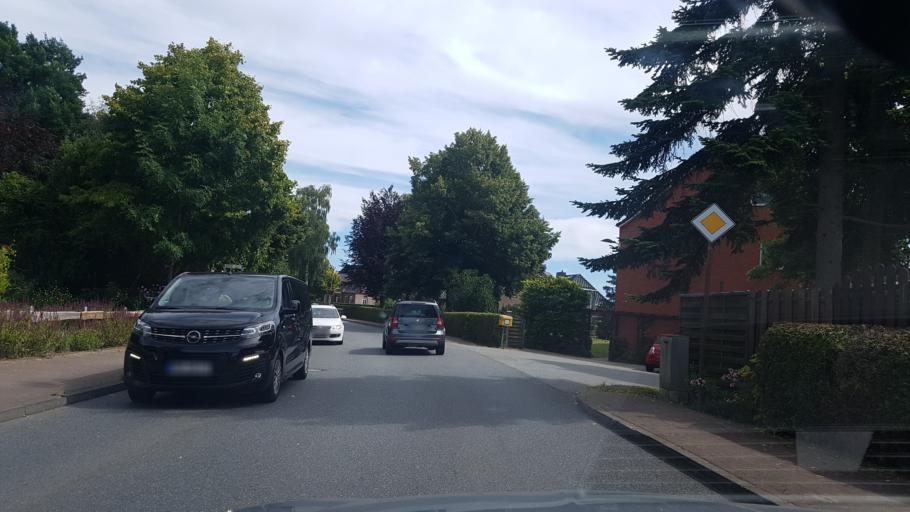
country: DE
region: Schleswig-Holstein
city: Gross Buchwald
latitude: 54.1619
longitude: 10.0834
